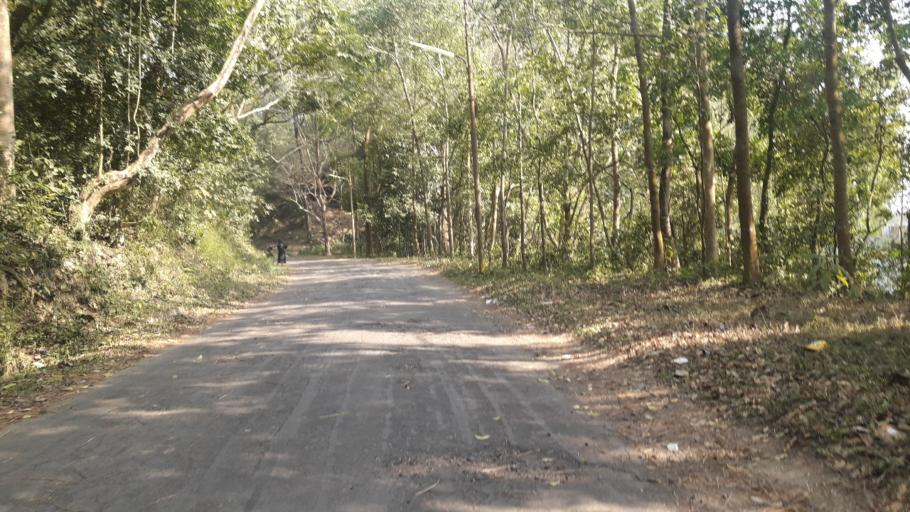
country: BD
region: Chittagong
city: Chittagong
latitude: 22.4665
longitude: 91.7898
